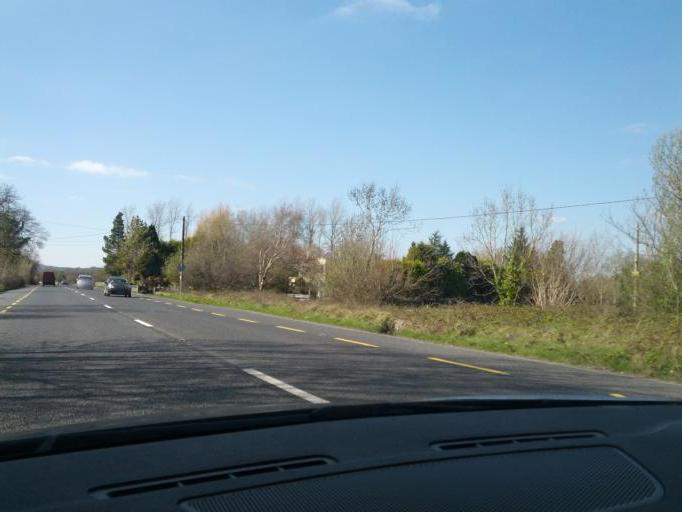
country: IE
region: Connaught
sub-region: County Galway
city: Bearna
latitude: 53.3070
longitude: -9.1199
